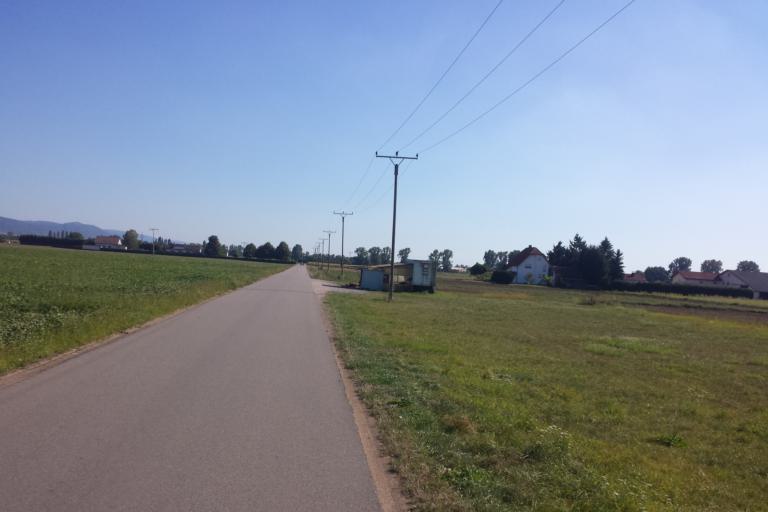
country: DE
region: Hesse
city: Viernheim
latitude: 49.5636
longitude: 8.5998
